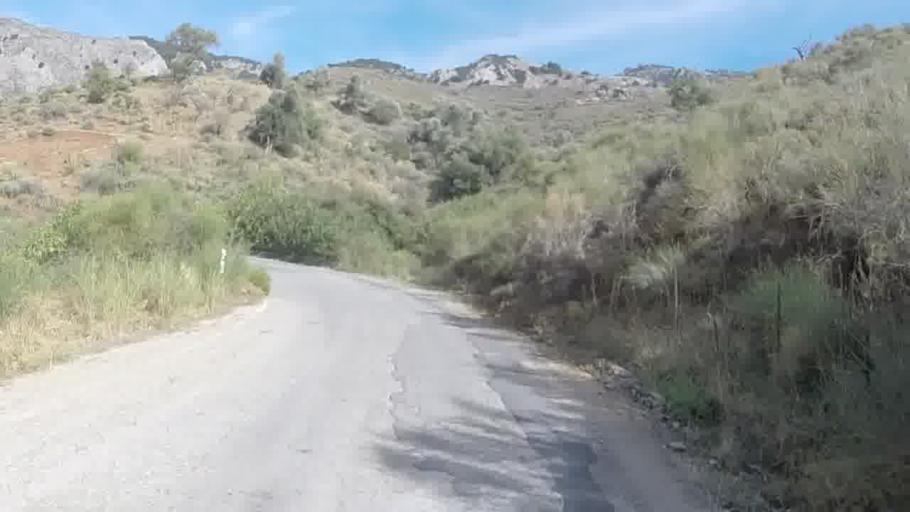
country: GR
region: Crete
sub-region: Nomos Rethymnis
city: Agia Galini
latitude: 35.1804
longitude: 24.7410
